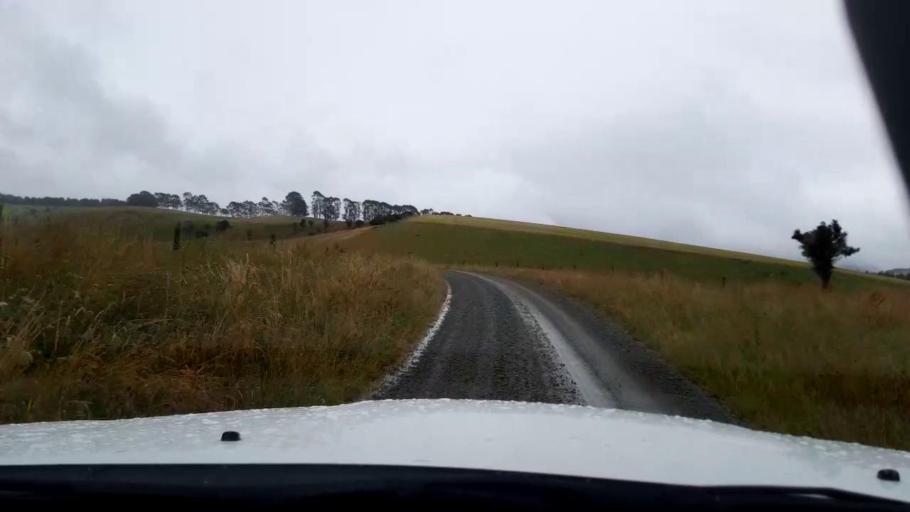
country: NZ
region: Canterbury
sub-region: Timaru District
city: Pleasant Point
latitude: -44.1749
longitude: 171.1130
